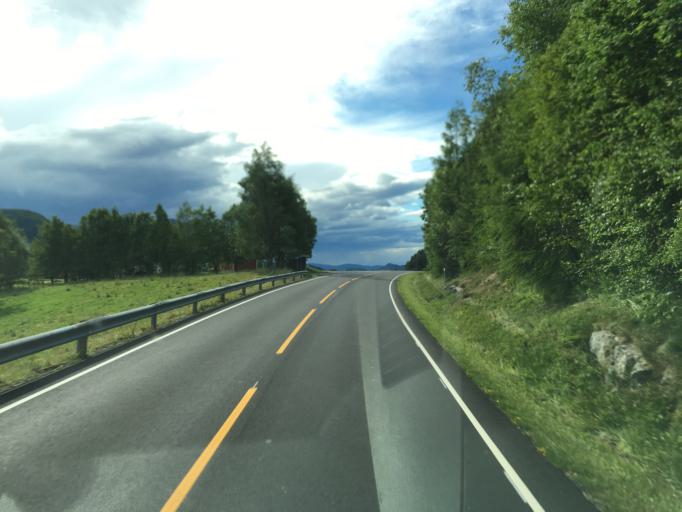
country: NO
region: More og Romsdal
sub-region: Tingvoll
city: Tingvoll
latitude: 62.9545
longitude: 8.1208
